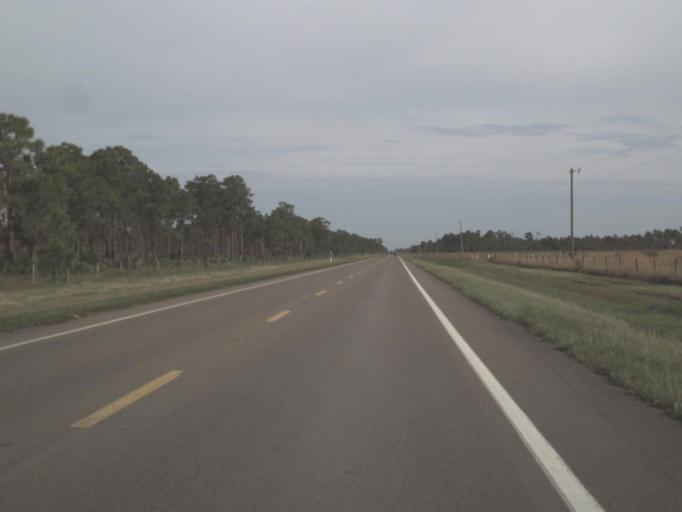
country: US
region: Florida
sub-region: Lee County
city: Olga
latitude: 26.8288
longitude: -81.7600
